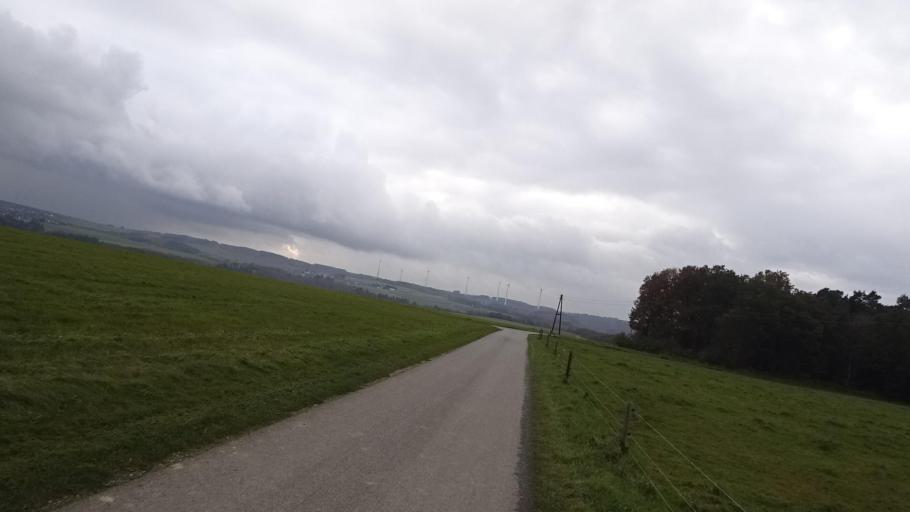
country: DE
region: Rheinland-Pfalz
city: Mermuth
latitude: 50.1484
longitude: 7.4731
